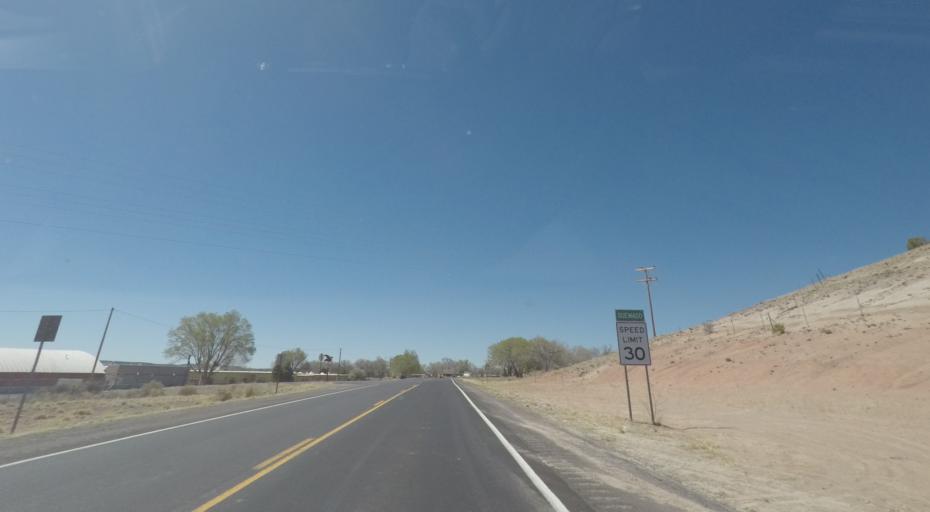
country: US
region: New Mexico
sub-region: Catron County
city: Reserve
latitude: 34.3402
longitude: -108.4908
